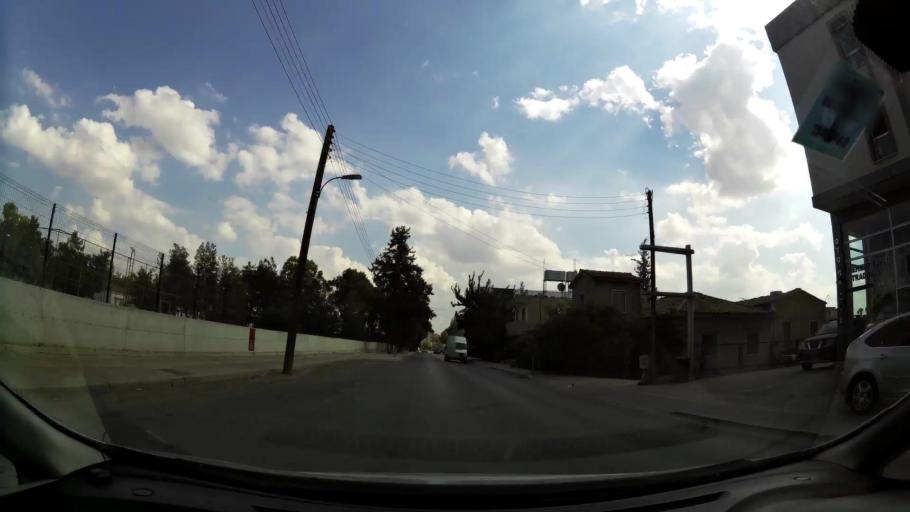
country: CY
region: Lefkosia
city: Nicosia
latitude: 35.2148
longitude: 33.3079
